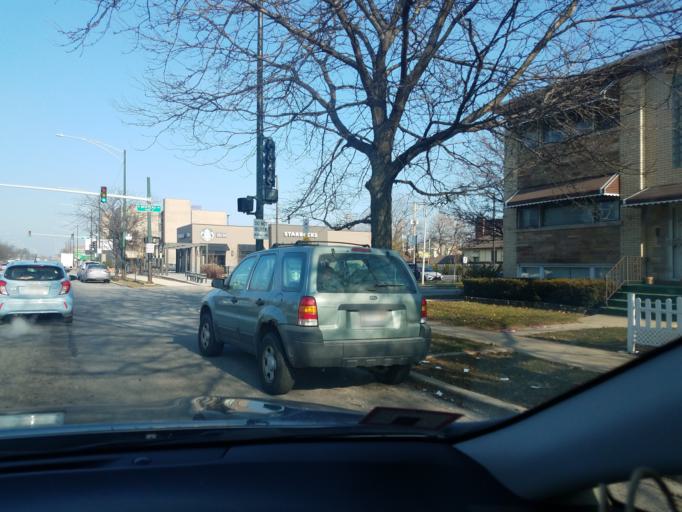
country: US
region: Illinois
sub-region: Cook County
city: Lincolnwood
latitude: 41.9562
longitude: -87.7473
